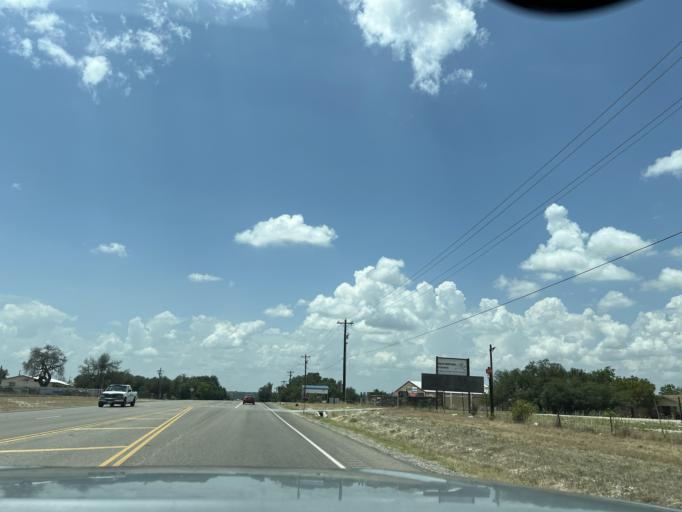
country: US
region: Texas
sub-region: Parker County
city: Weatherford
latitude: 32.8234
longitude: -97.7728
